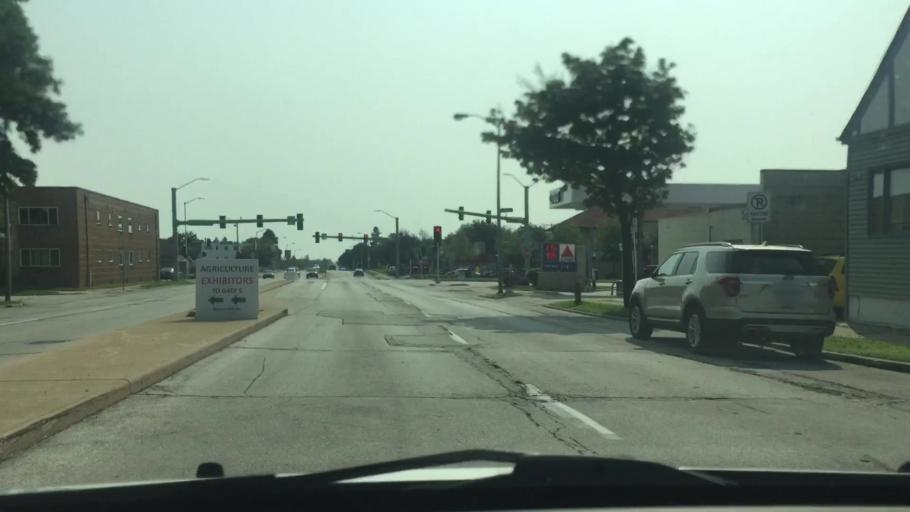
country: US
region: Wisconsin
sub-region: Milwaukee County
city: West Allis
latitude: 43.0025
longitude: -88.0328
